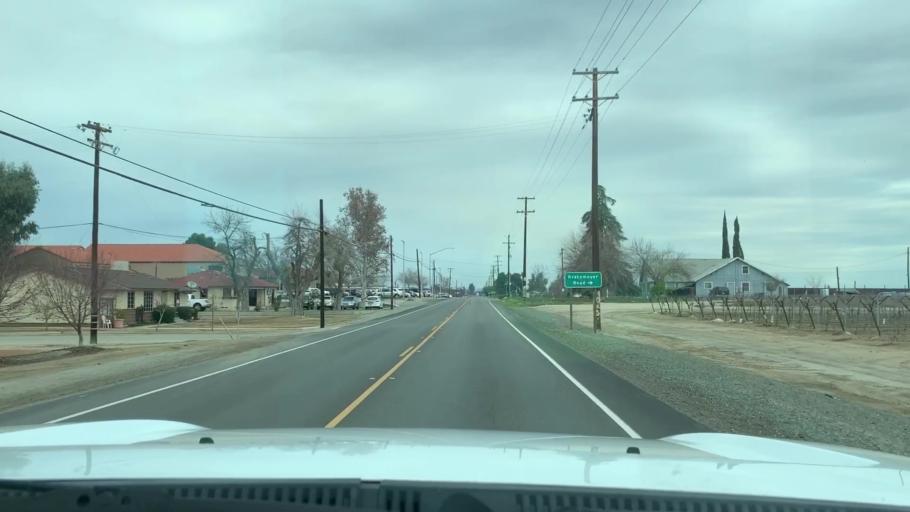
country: US
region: California
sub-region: Kern County
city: Shafter
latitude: 35.4186
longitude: -119.2519
